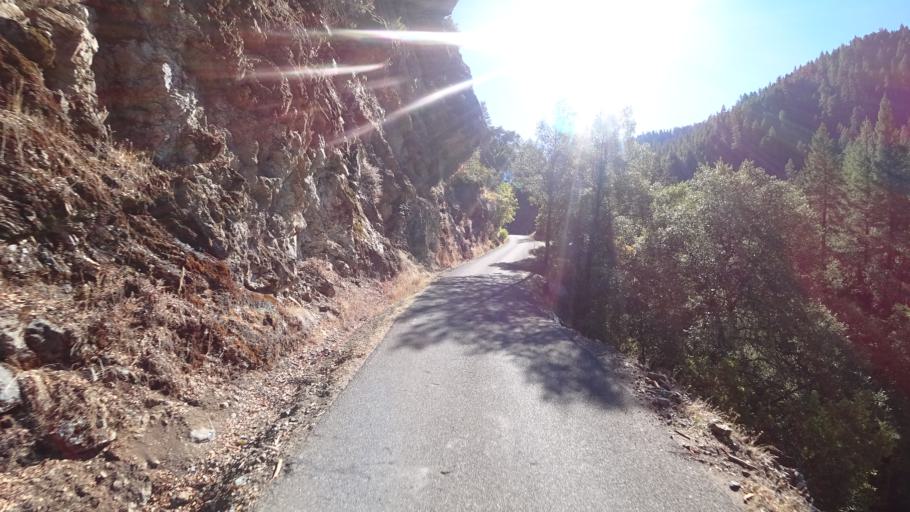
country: US
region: California
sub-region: Humboldt County
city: Willow Creek
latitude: 41.1457
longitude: -123.1947
